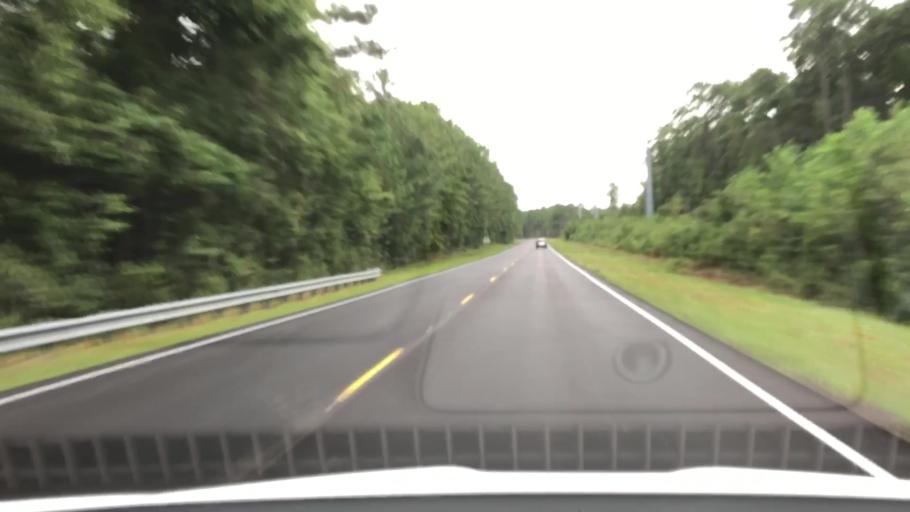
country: US
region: North Carolina
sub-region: Carteret County
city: Cape Carteret
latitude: 34.7669
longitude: -77.0964
